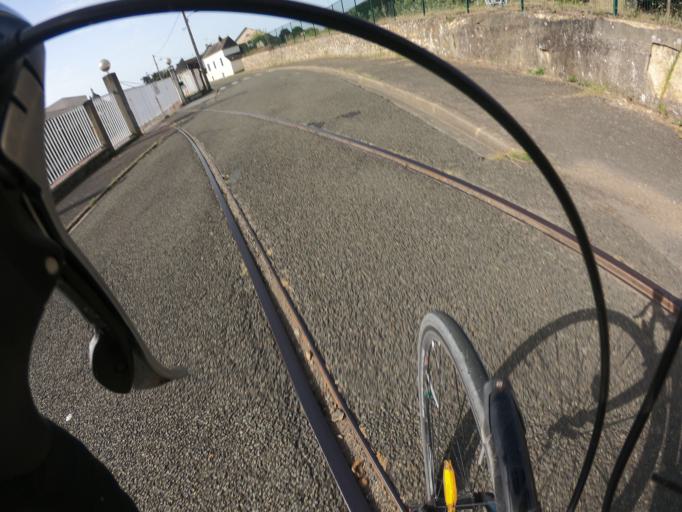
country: FR
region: Centre
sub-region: Departement d'Eure-et-Loir
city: Margon
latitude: 48.3277
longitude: 0.8123
